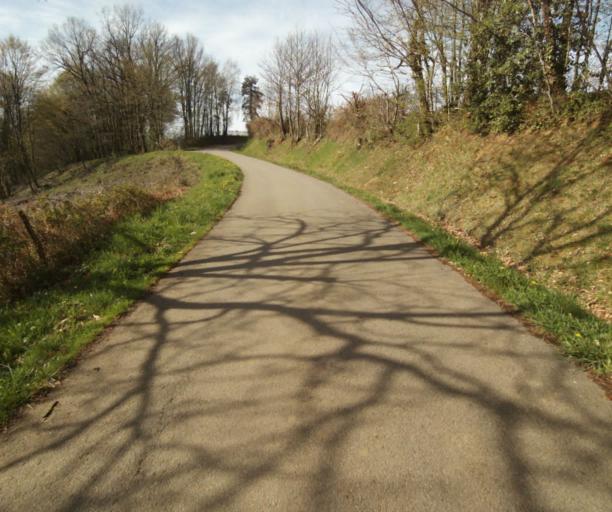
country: FR
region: Limousin
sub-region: Departement de la Correze
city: Laguenne
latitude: 45.2588
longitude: 1.8166
